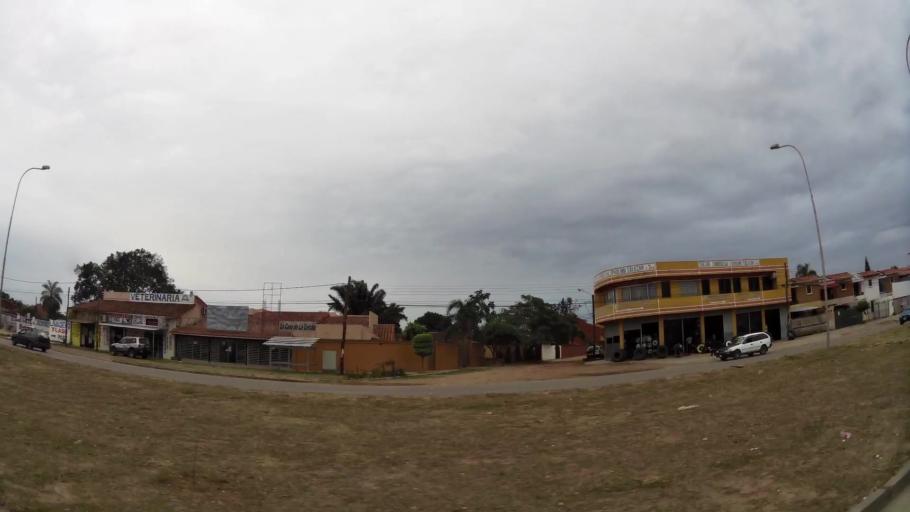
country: BO
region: Santa Cruz
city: Santa Cruz de la Sierra
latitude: -17.8374
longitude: -63.1829
